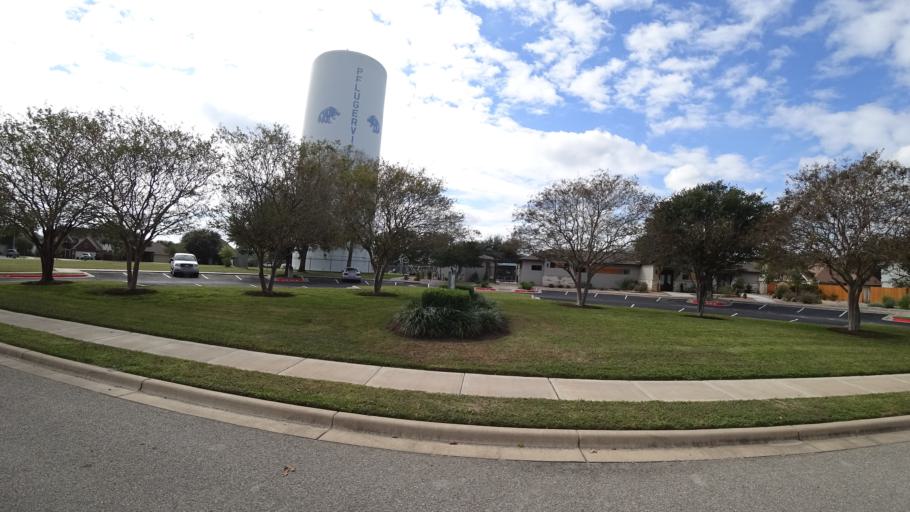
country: US
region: Texas
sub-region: Travis County
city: Windemere
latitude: 30.4397
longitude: -97.6413
